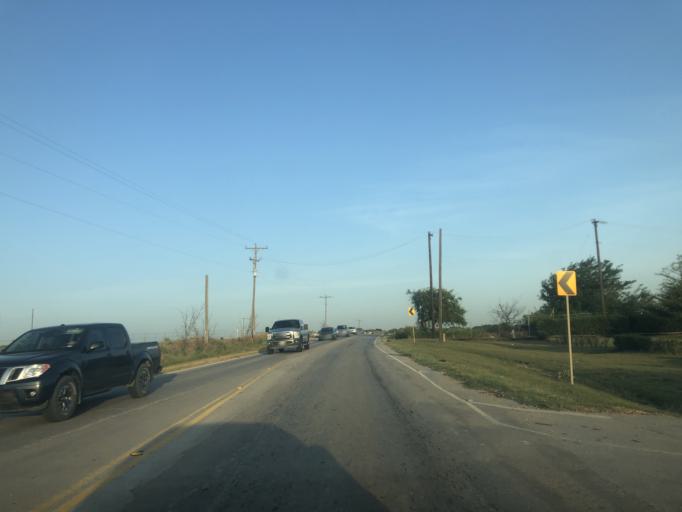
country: US
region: Texas
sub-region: Tarrant County
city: White Settlement
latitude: 32.7744
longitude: -97.4825
